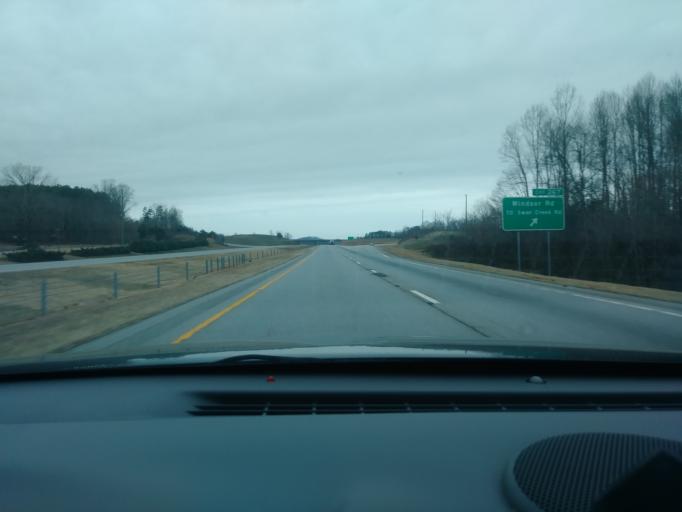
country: US
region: North Carolina
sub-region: Yadkin County
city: Jonesville
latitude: 36.1286
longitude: -80.8357
